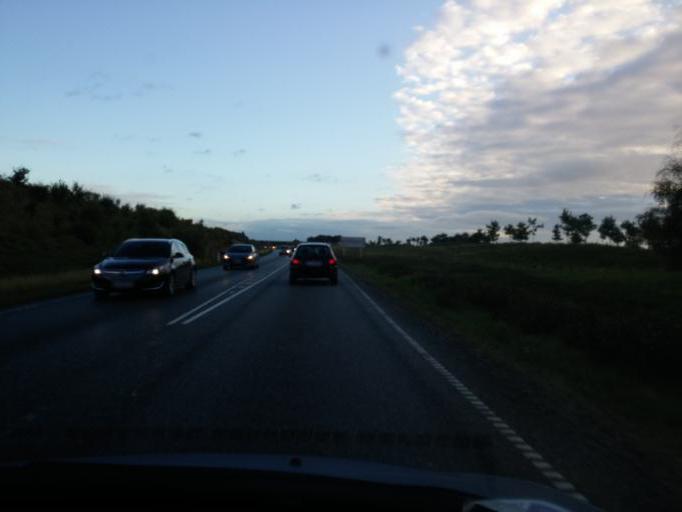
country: DK
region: South Denmark
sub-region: Odense Kommune
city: Neder Holluf
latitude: 55.3708
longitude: 10.4740
